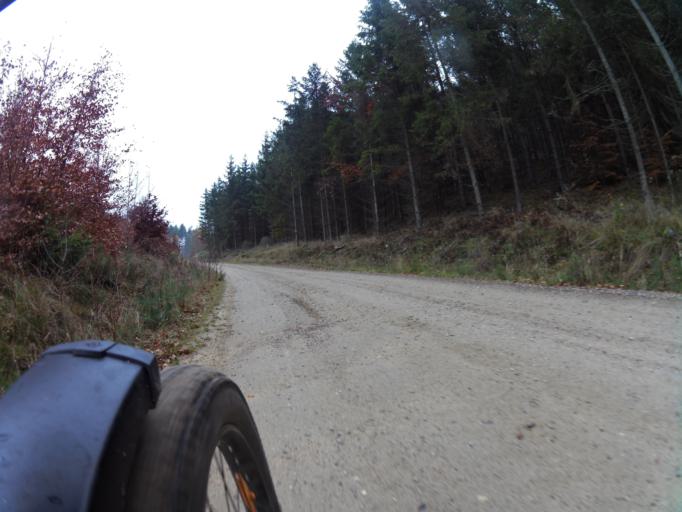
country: PL
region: Pomeranian Voivodeship
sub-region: Powiat wejherowski
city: Orle
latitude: 54.7084
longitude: 18.1465
